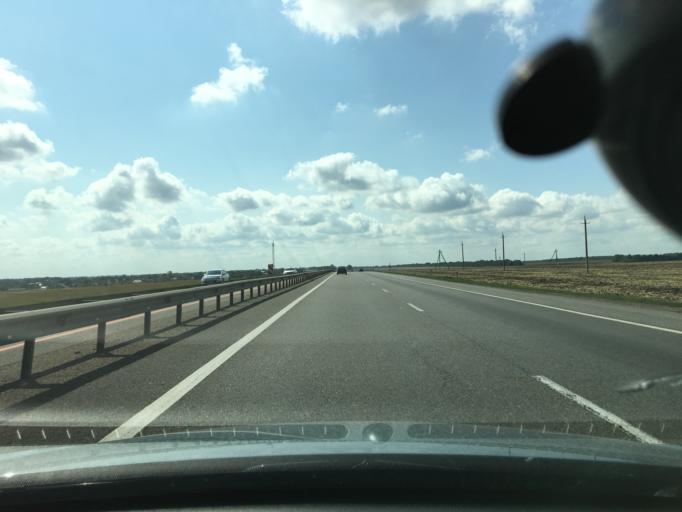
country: RU
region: Krasnodarskiy
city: Krasnoye
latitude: 46.7231
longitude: 39.6548
